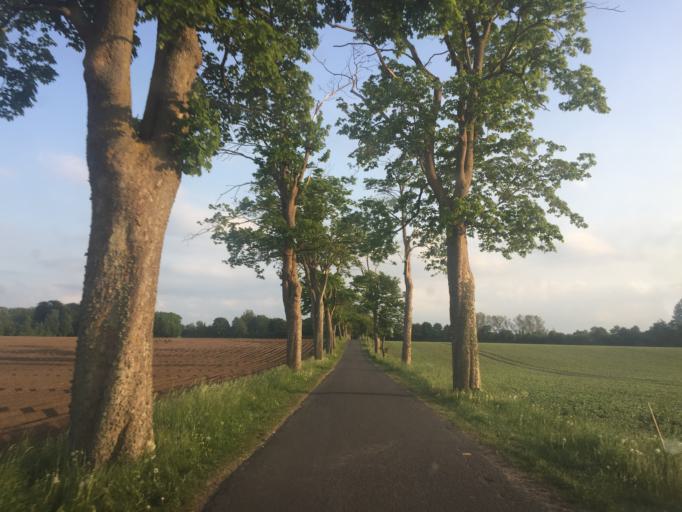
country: DK
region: South Denmark
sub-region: Kerteminde Kommune
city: Langeskov
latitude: 55.3514
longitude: 10.5247
